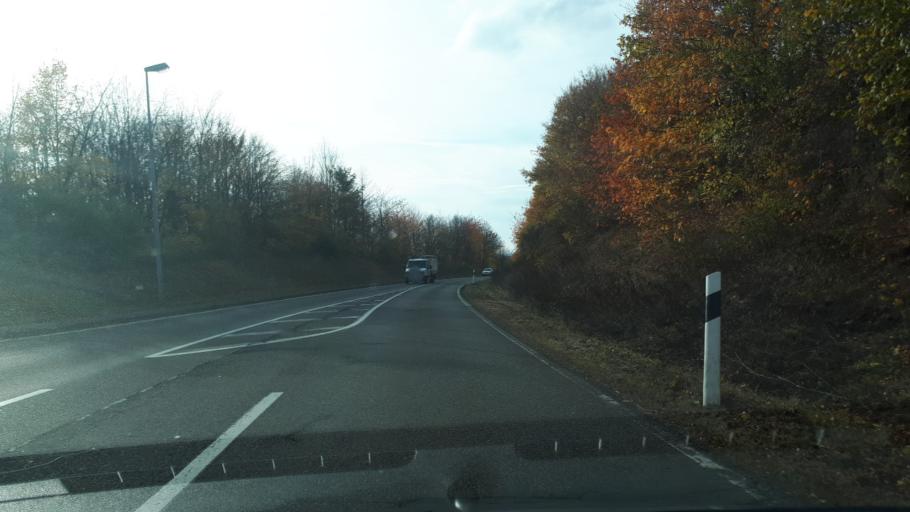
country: DE
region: Rheinland-Pfalz
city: Mullenbach
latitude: 50.2255
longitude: 7.0711
